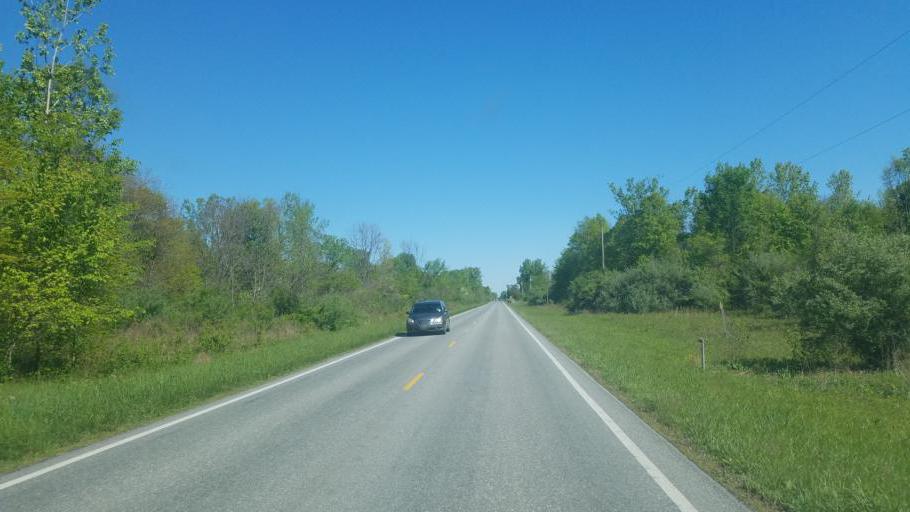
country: US
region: Ohio
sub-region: Delaware County
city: Lewis Center
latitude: 40.2064
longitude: -82.9481
